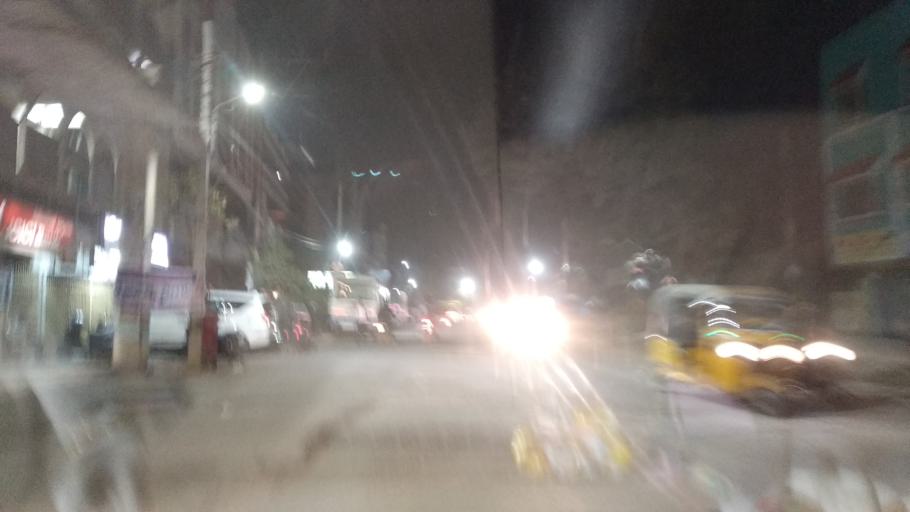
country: IN
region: Telangana
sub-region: Rangareddi
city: Kukatpalli
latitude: 17.4540
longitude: 78.4175
